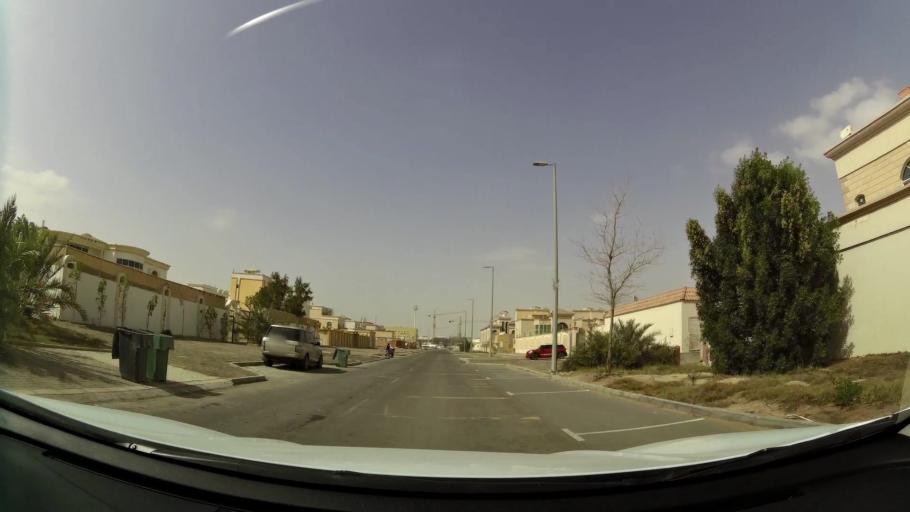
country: AE
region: Abu Dhabi
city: Abu Dhabi
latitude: 24.4251
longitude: 54.5848
